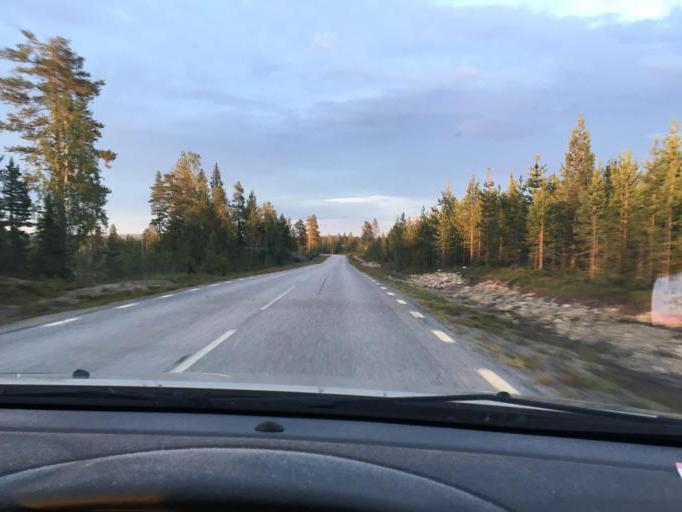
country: SE
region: Norrbotten
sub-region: Kalix Kommun
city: Toere
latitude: 66.0537
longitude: 22.4684
